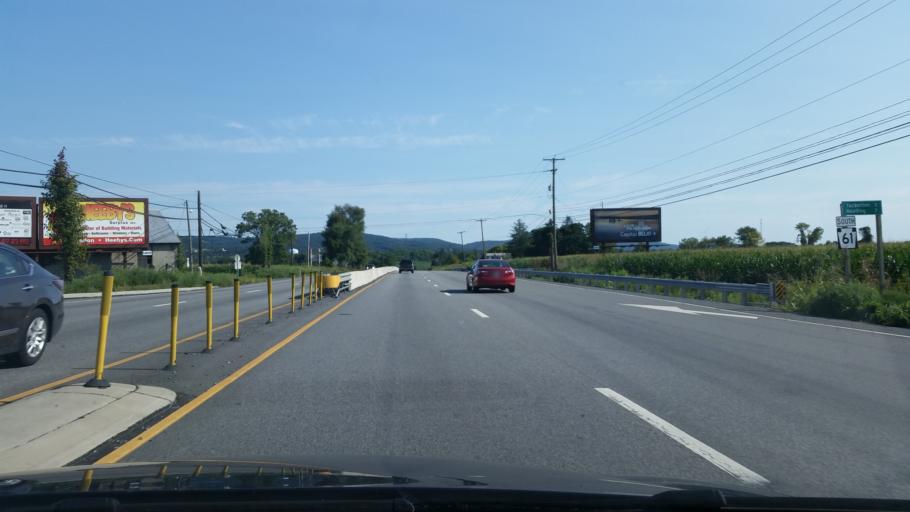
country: US
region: Pennsylvania
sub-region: Berks County
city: Leesport
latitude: 40.4384
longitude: -75.9441
